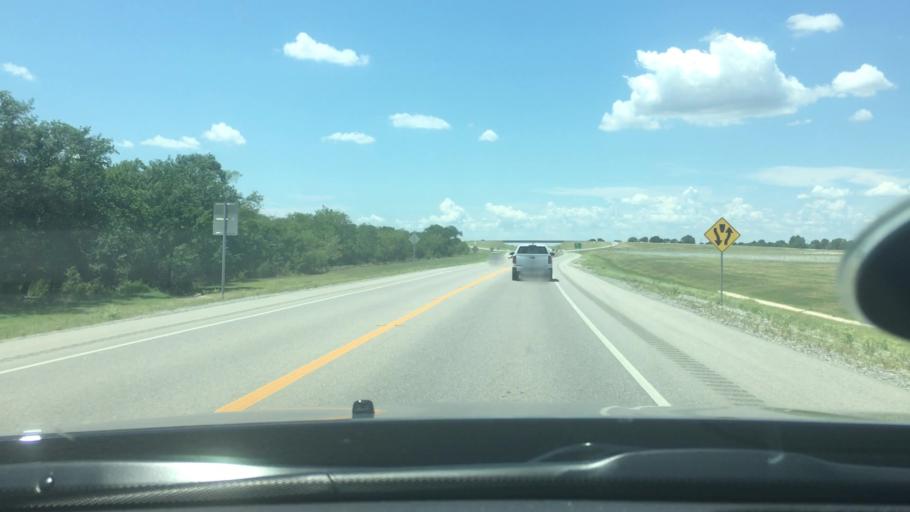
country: US
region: Oklahoma
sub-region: Bryan County
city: Durant
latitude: 33.9653
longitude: -96.3596
